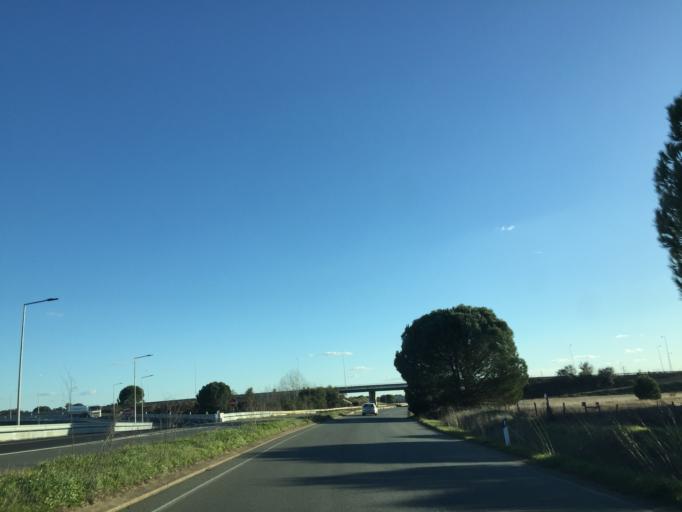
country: PT
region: Setubal
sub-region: Grandola
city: Grandola
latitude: 38.1150
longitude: -8.4184
